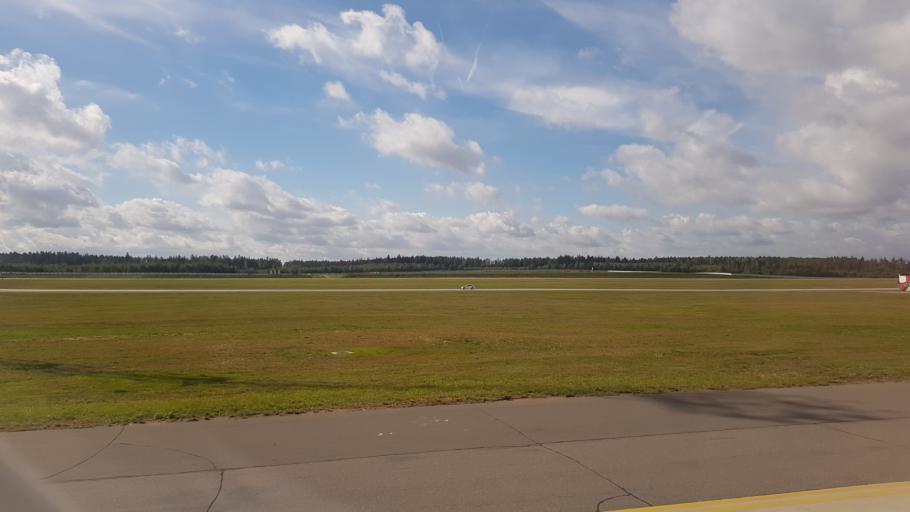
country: BY
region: Minsk
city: Smilavichy
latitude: 53.8865
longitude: 28.0329
